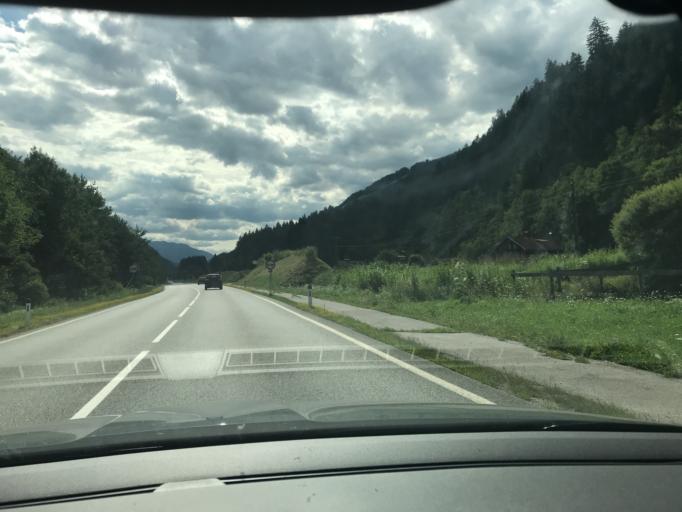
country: AT
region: Tyrol
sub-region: Politischer Bezirk Lienz
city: Obertilliach
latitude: 46.7805
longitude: 12.6430
